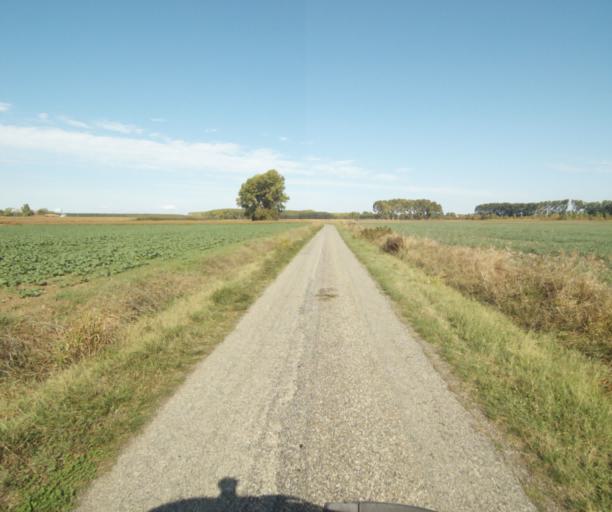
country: FR
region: Midi-Pyrenees
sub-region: Departement du Tarn-et-Garonne
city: Finhan
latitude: 43.8930
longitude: 1.2212
